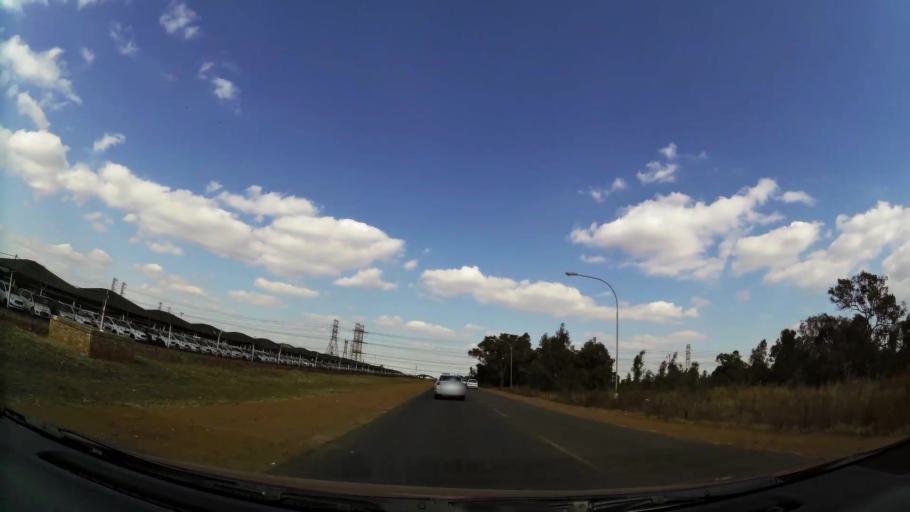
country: ZA
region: Gauteng
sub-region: Ekurhuleni Metropolitan Municipality
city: Tembisa
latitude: -26.0105
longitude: 28.2520
